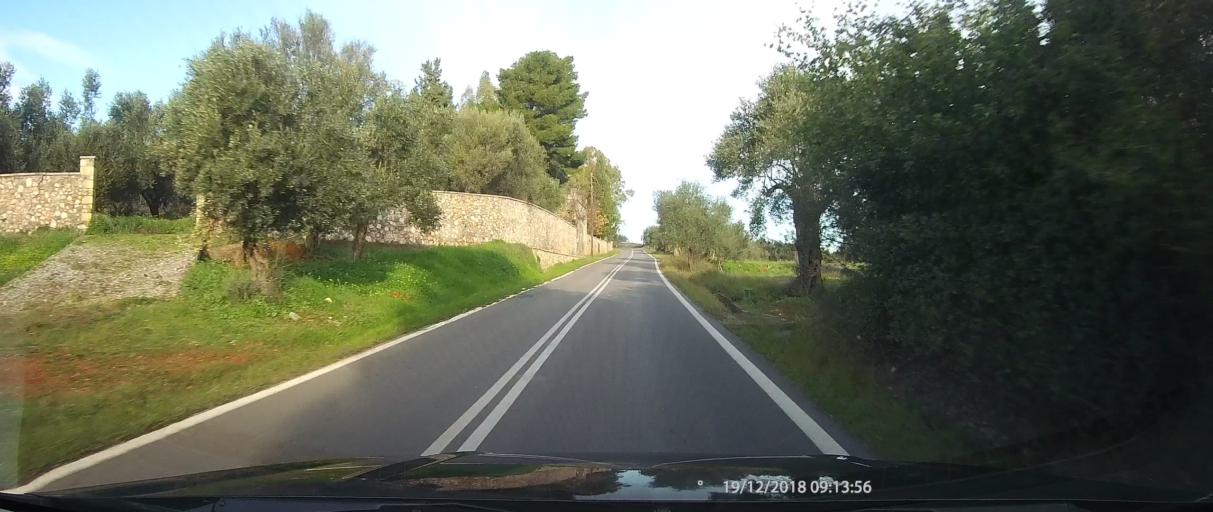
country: GR
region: Peloponnese
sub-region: Nomos Lakonias
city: Magoula
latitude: 37.0833
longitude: 22.3932
